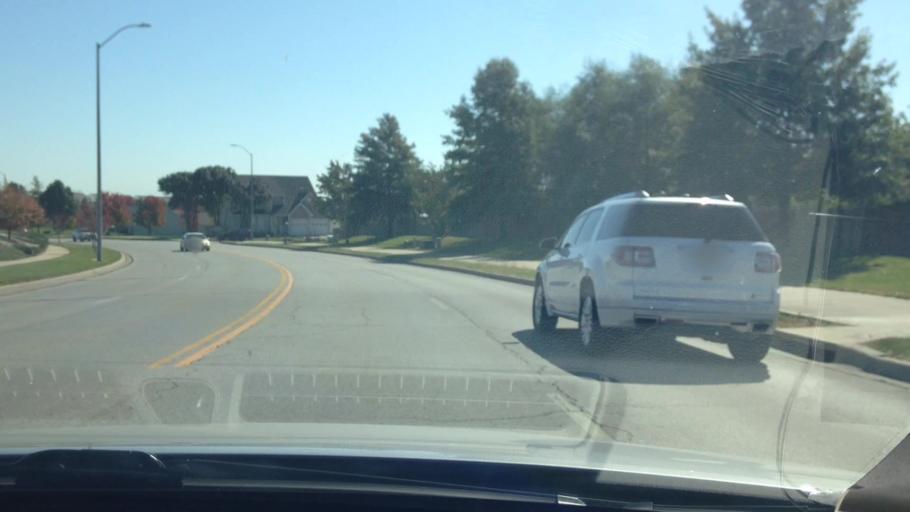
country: US
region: Missouri
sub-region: Platte County
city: Platte City
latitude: 39.3501
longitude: -94.7643
